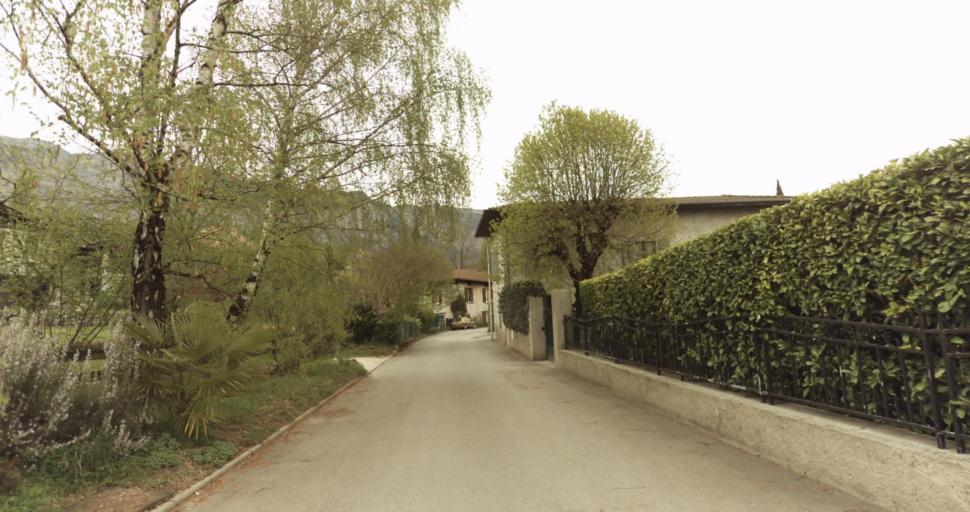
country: FR
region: Rhone-Alpes
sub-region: Departement de l'Isere
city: Montbonnot-Saint-Martin
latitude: 45.2291
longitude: 5.8199
